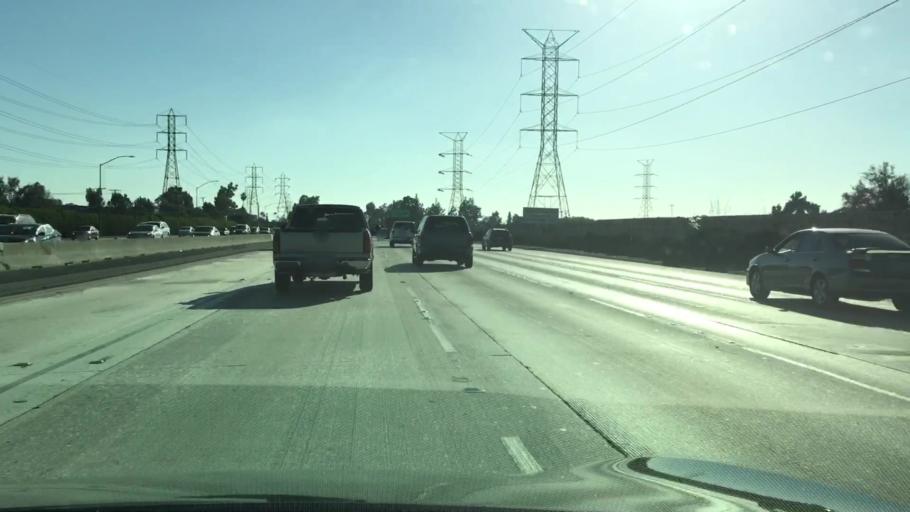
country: US
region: California
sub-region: Los Angeles County
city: South El Monte
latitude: 34.0206
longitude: -118.0472
